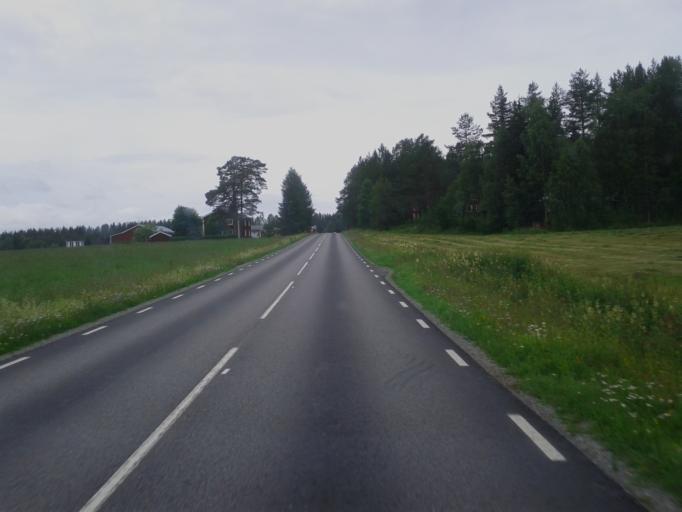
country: SE
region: Vaesterbotten
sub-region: Skelleftea Kommun
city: Viken
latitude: 64.8841
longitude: 20.7670
